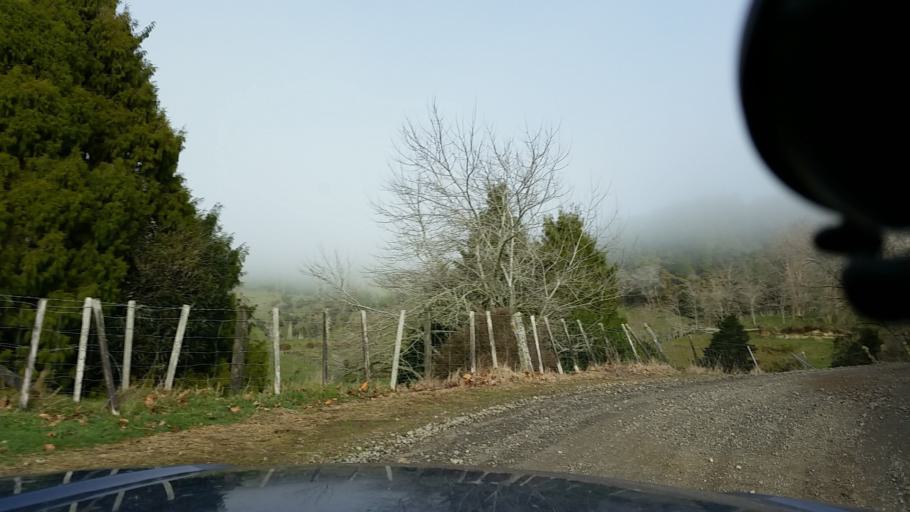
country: NZ
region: Taranaki
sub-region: New Plymouth District
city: Waitara
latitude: -39.0006
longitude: 174.7676
